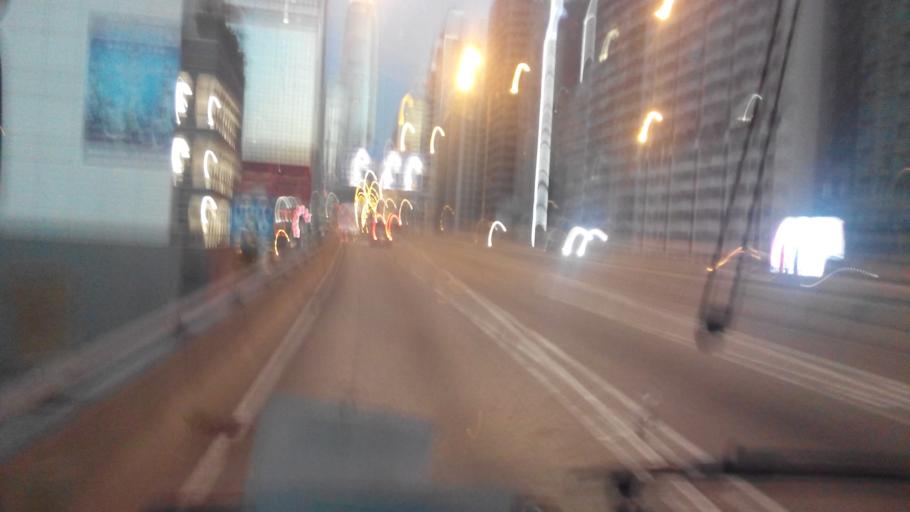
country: HK
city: Hong Kong
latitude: 22.2886
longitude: 114.1481
